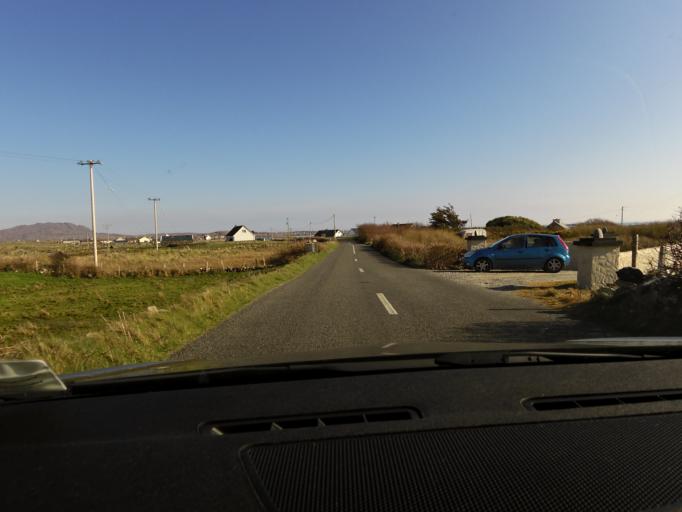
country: IE
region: Connaught
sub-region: County Galway
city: Clifden
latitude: 53.4182
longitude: -10.0598
